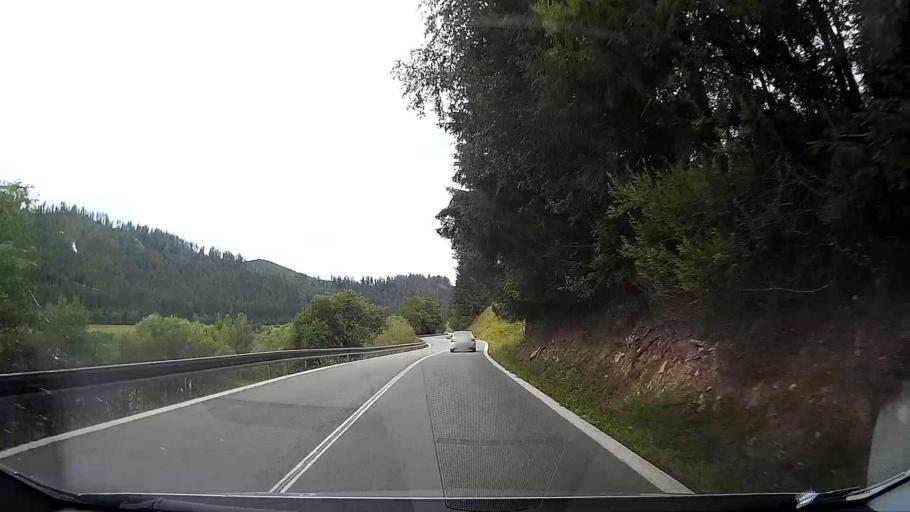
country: SK
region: Banskobystricky
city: Revuca
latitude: 48.8313
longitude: 20.1702
